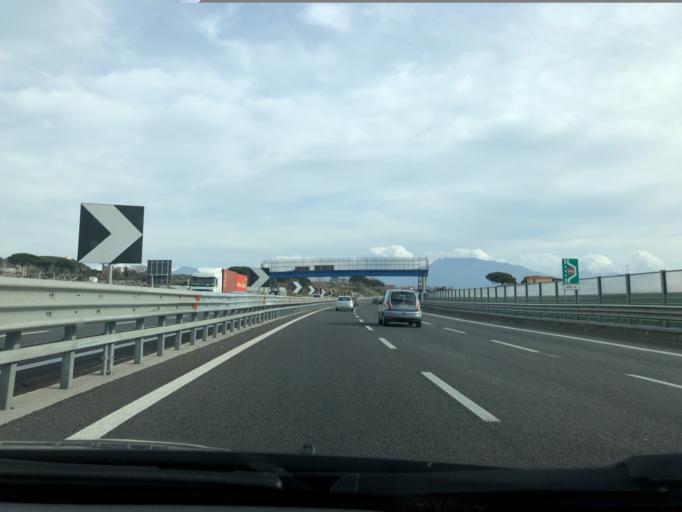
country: IT
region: Campania
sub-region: Provincia di Napoli
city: Torre del Greco
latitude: 40.7854
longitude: 14.3866
